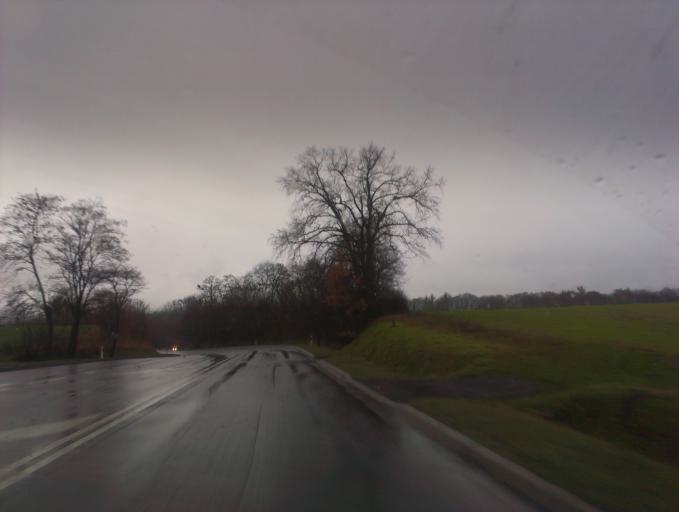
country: PL
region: Greater Poland Voivodeship
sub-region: Powiat pilski
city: Ujscie
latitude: 53.0462
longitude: 16.7501
